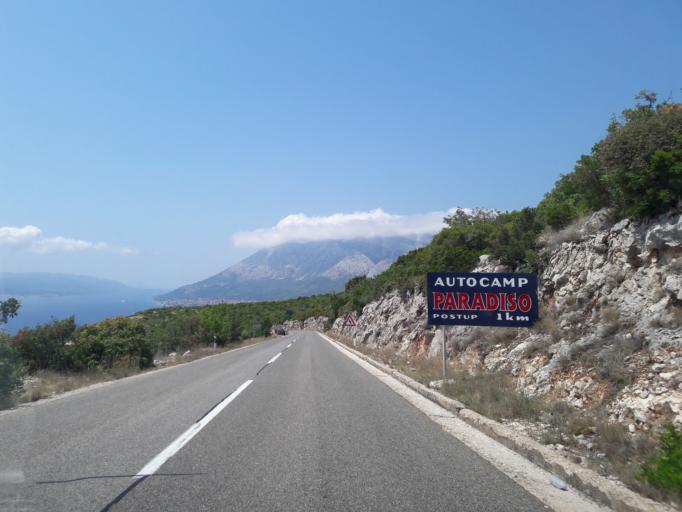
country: HR
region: Dubrovacko-Neretvanska
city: Orebic
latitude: 42.9706
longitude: 17.2466
